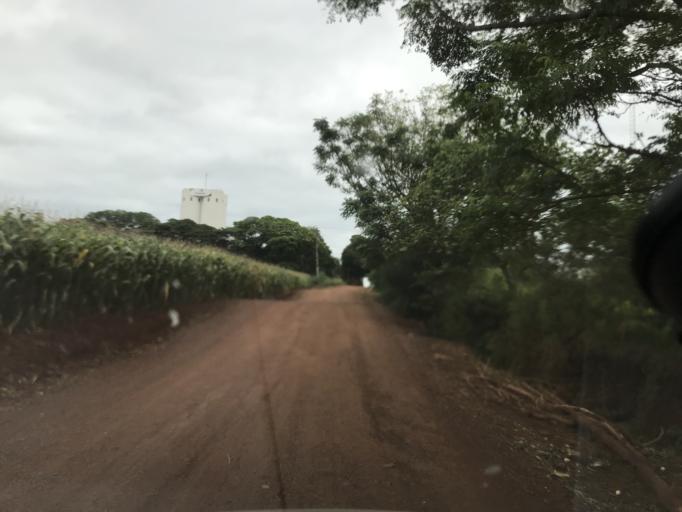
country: BR
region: Parana
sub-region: Palotina
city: Palotina
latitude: -24.3041
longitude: -53.8319
